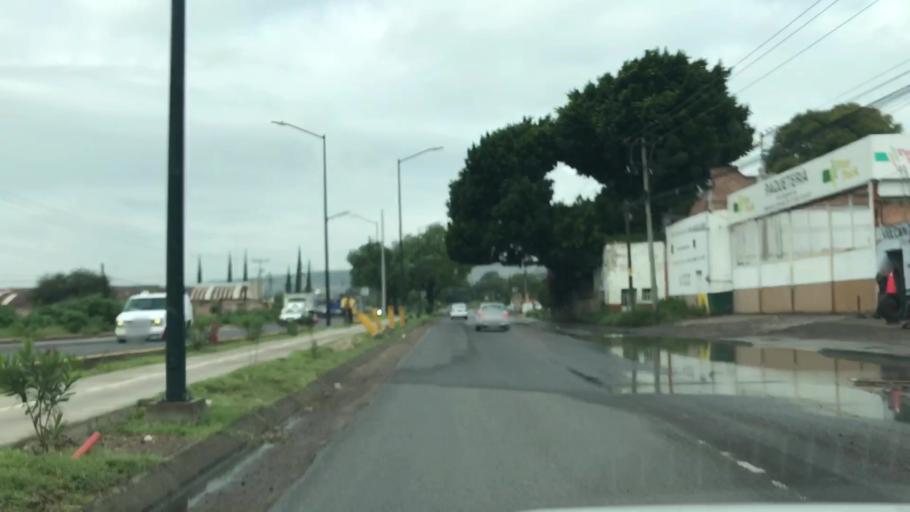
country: MX
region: Guanajuato
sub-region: Leon
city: Malagana (San Antonio del Monte)
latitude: 21.0888
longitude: -101.7407
